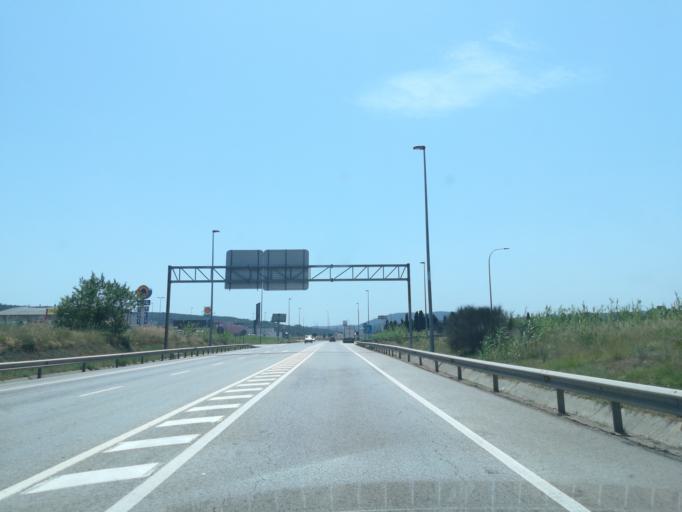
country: ES
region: Catalonia
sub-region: Provincia de Girona
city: la Jonquera
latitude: 42.4071
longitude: 2.8779
